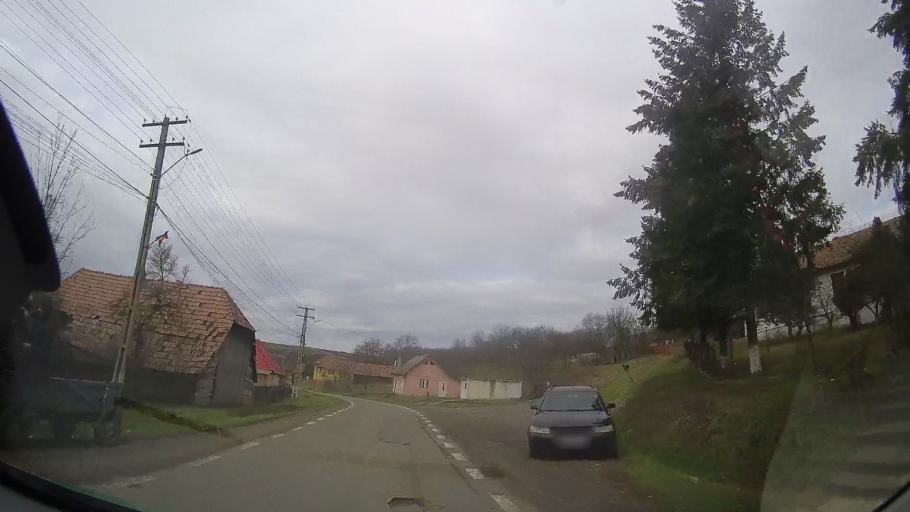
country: RO
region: Mures
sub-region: Comuna Cozma
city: Cozma
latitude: 46.8090
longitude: 24.5204
